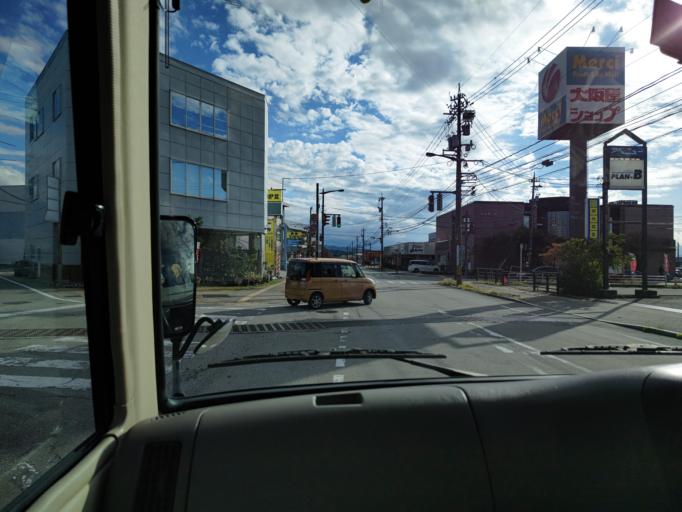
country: JP
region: Toyama
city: Uozu
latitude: 36.8708
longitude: 137.4470
